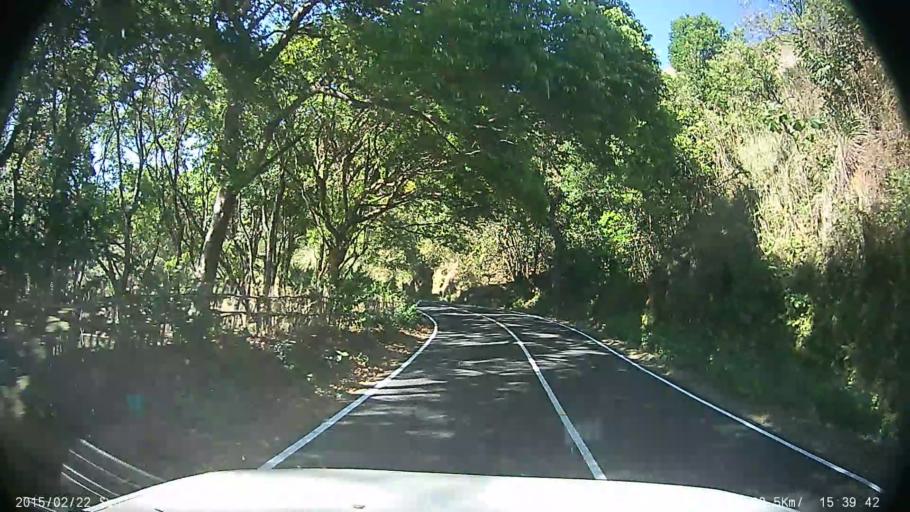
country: IN
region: Kerala
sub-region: Kottayam
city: Erattupetta
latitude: 9.5661
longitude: 76.9778
